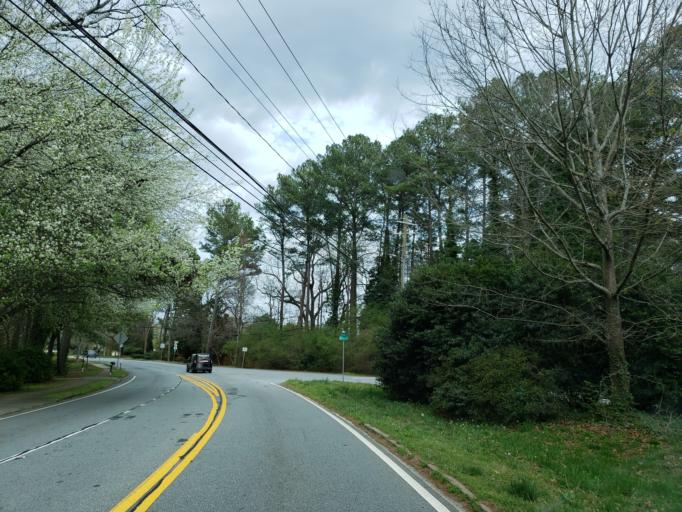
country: US
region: Georgia
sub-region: DeKalb County
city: North Druid Hills
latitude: 33.8201
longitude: -84.3026
